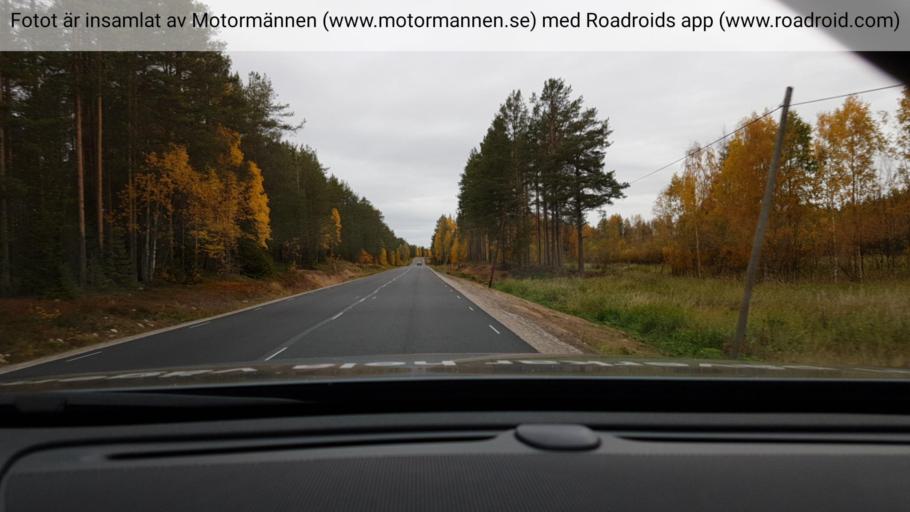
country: SE
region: Norrbotten
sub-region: Overkalix Kommun
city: OEverkalix
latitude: 66.4365
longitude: 22.7923
